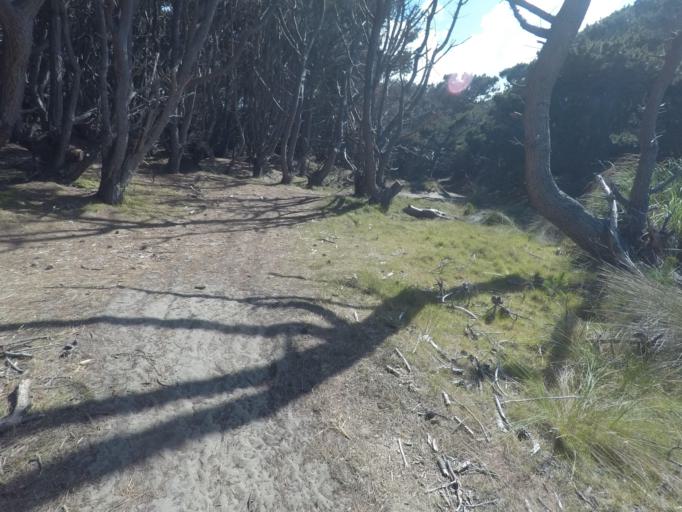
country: NZ
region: Auckland
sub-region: Auckland
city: Parakai
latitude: -36.6058
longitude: 174.2711
